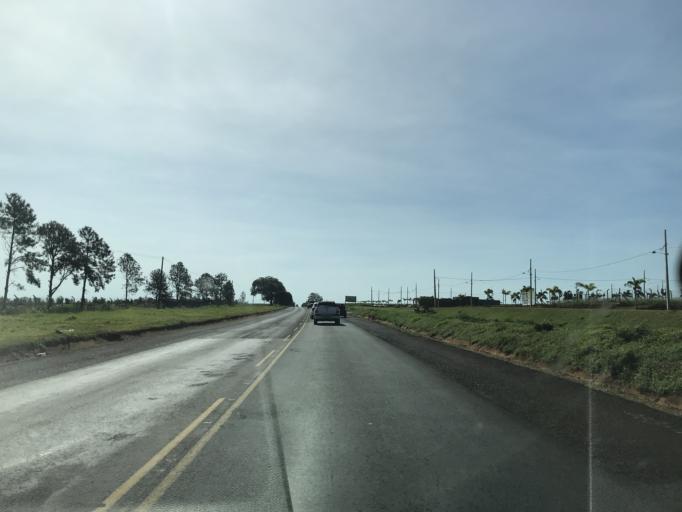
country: BR
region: Parana
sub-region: Maringa
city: Maringa
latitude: -23.2429
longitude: -51.8633
